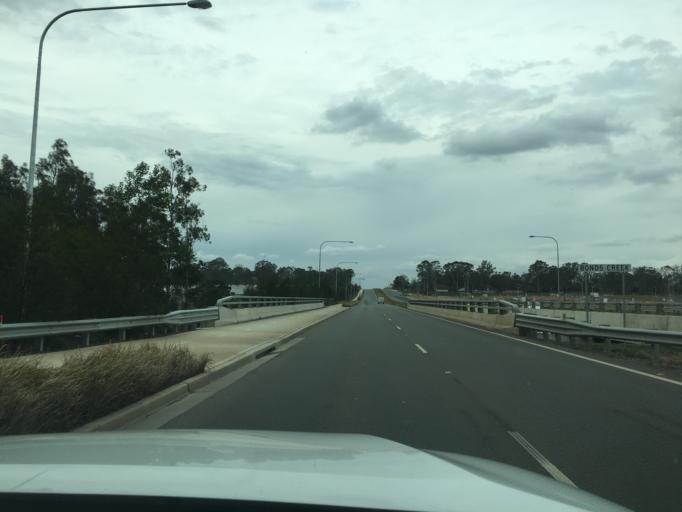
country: AU
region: New South Wales
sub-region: Campbelltown Municipality
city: Denham Court
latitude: -33.9618
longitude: 150.8201
